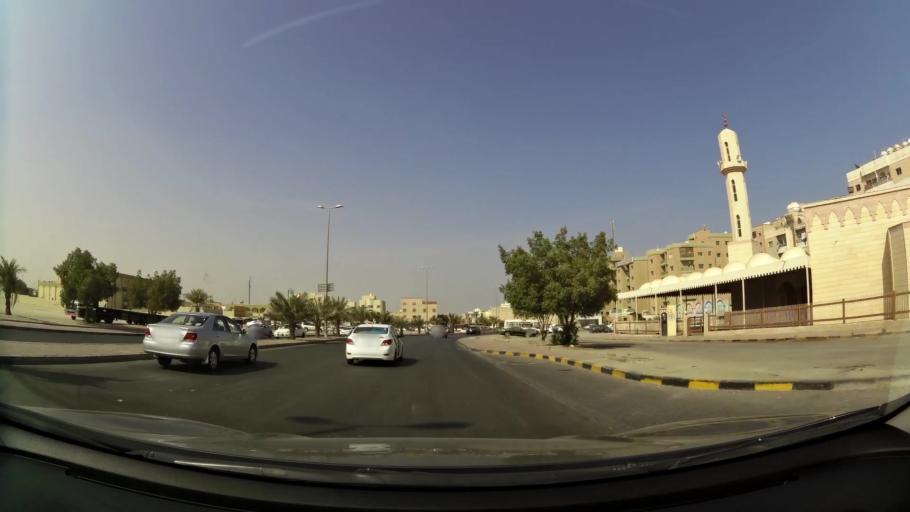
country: KW
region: Al Ahmadi
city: Al Manqaf
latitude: 29.1051
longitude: 48.1240
